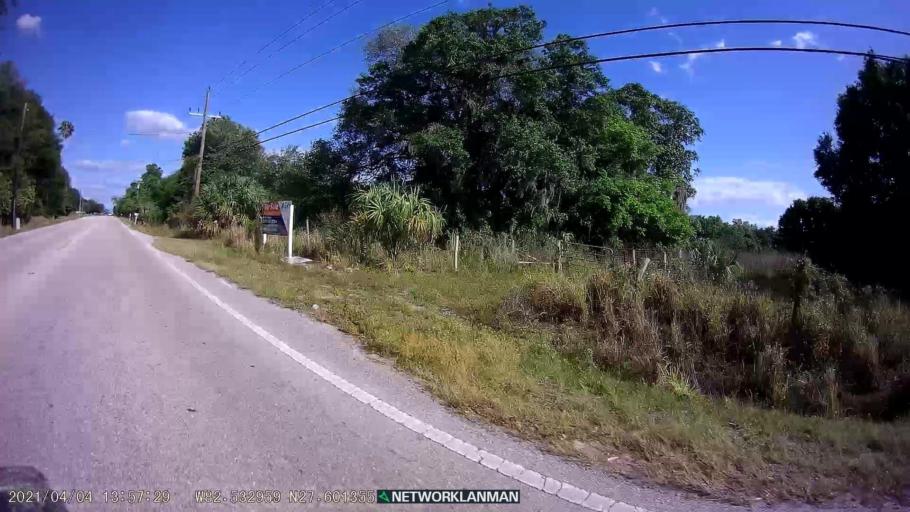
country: US
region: Florida
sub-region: Manatee County
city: Memphis
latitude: 27.6009
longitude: -82.5328
